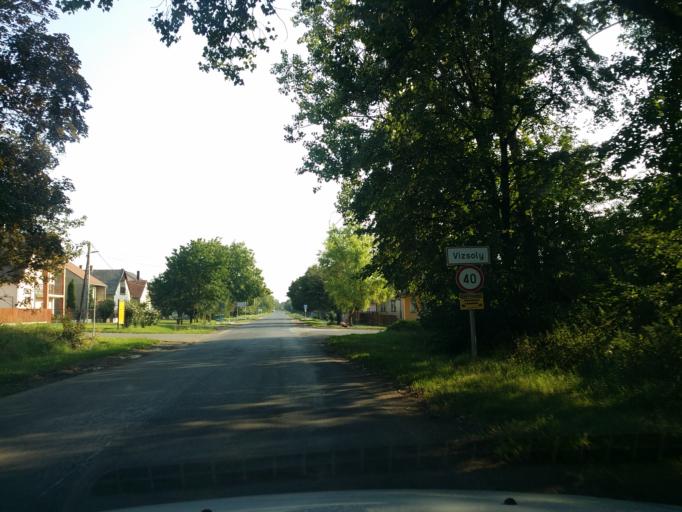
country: HU
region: Borsod-Abauj-Zemplen
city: Gonc
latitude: 48.3932
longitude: 21.2222
